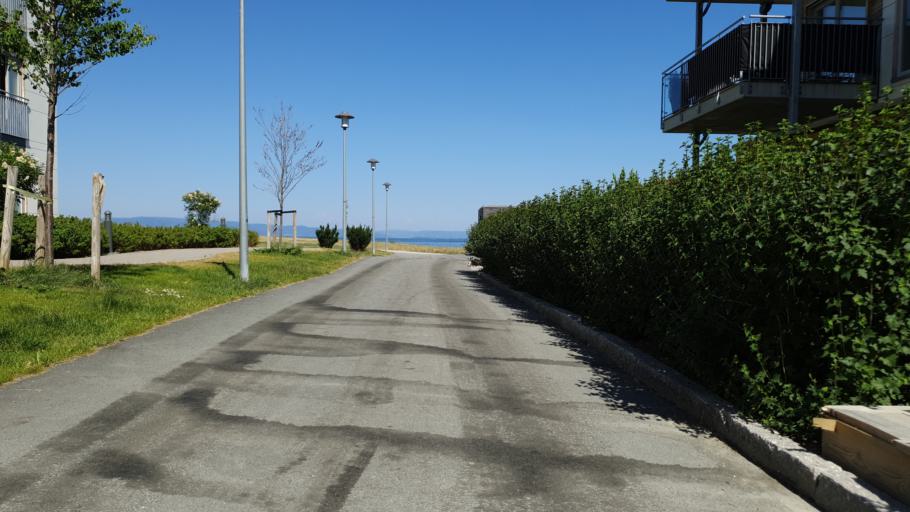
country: NO
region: Sor-Trondelag
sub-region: Trondheim
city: Trondheim
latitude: 63.4300
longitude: 10.5273
